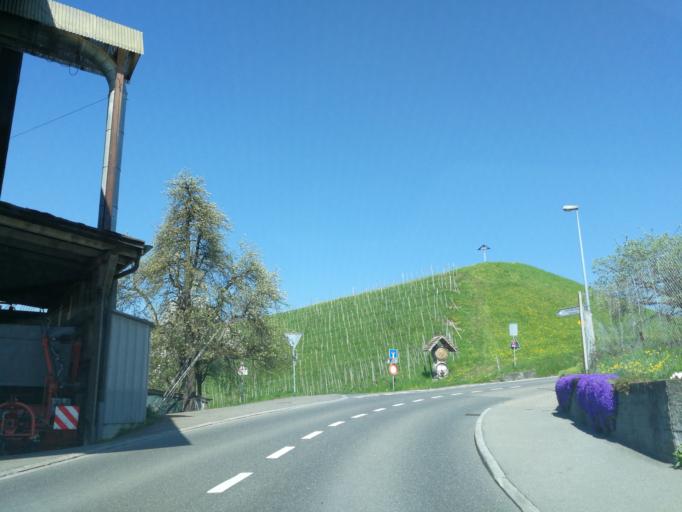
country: CH
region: Saint Gallen
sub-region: Wahlkreis See-Gaster
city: Rapperswil
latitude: 47.2446
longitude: 8.8182
